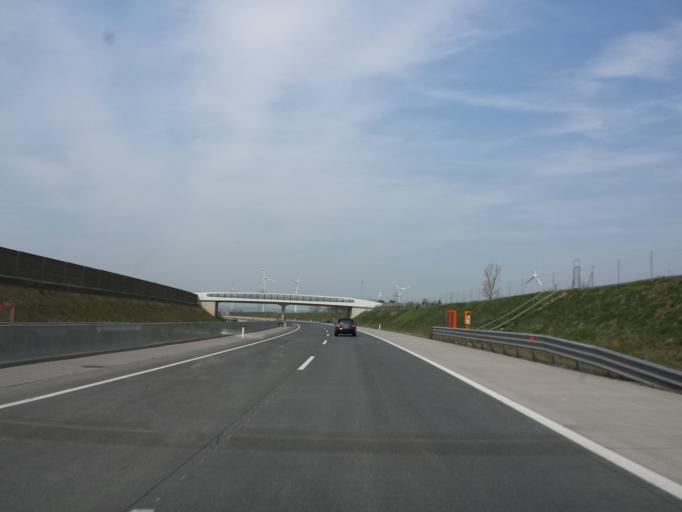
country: AT
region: Lower Austria
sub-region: Politischer Bezirk Mistelbach
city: Pillichsdorf
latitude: 48.3318
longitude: 16.5148
